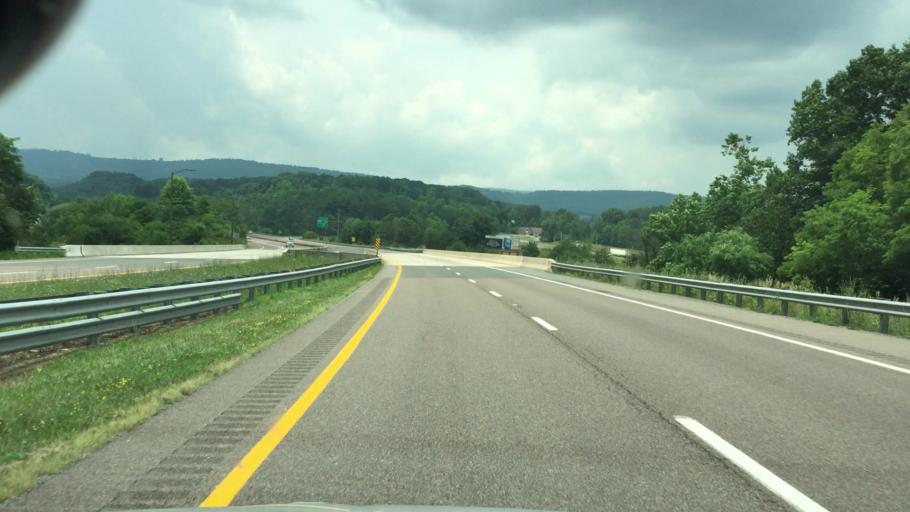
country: US
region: Maryland
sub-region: Allegany County
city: Cumberland
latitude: 39.7044
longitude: -78.5656
